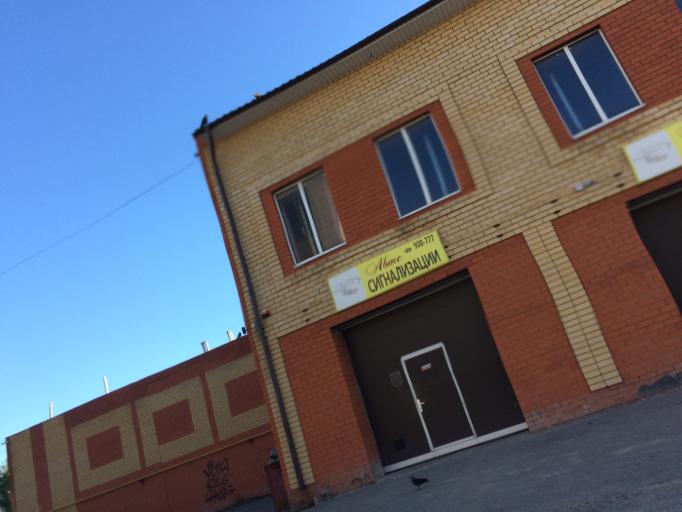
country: RU
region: Mariy-El
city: Medvedevo
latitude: 56.6424
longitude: 47.8337
